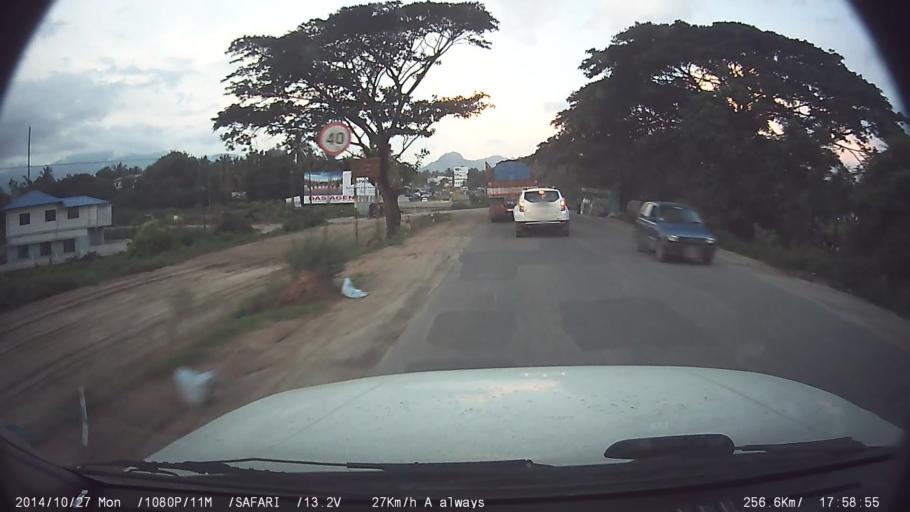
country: IN
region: Kerala
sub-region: Palakkad district
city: Palakkad
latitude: 10.7650
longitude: 76.6763
